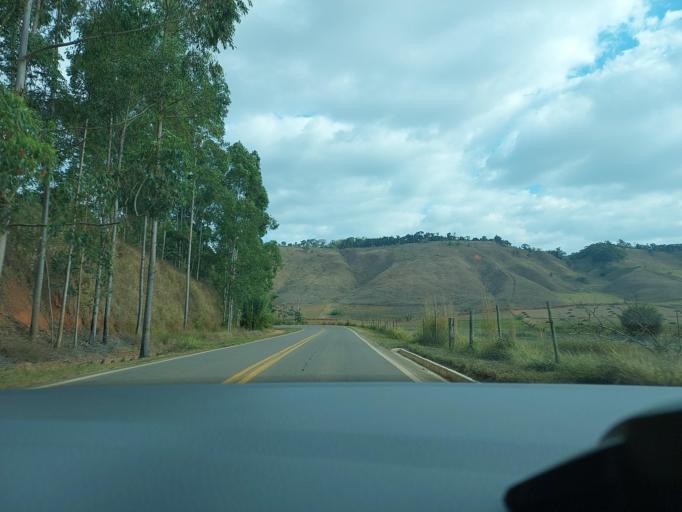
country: BR
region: Minas Gerais
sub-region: Visconde Do Rio Branco
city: Visconde do Rio Branco
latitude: -20.8729
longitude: -42.6687
